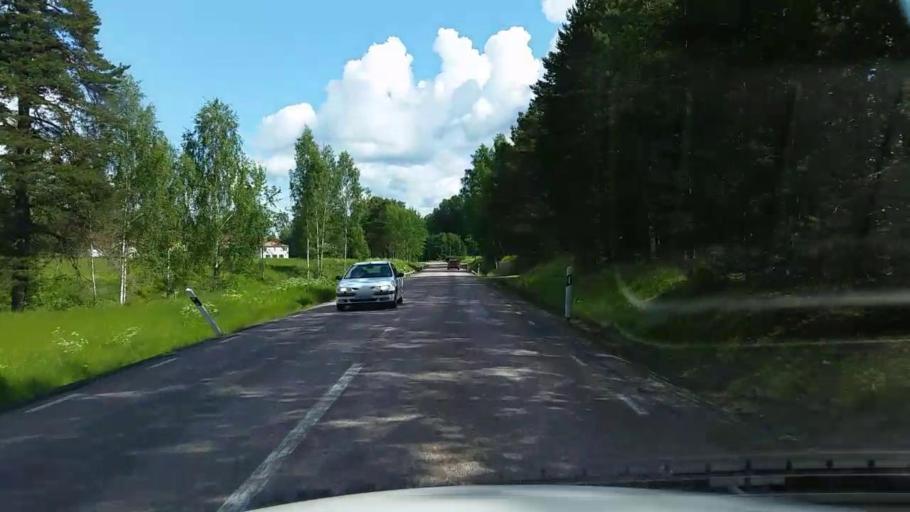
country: SE
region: Vaestmanland
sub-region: Kopings Kommun
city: Kolsva
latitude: 59.7025
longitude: 15.7892
